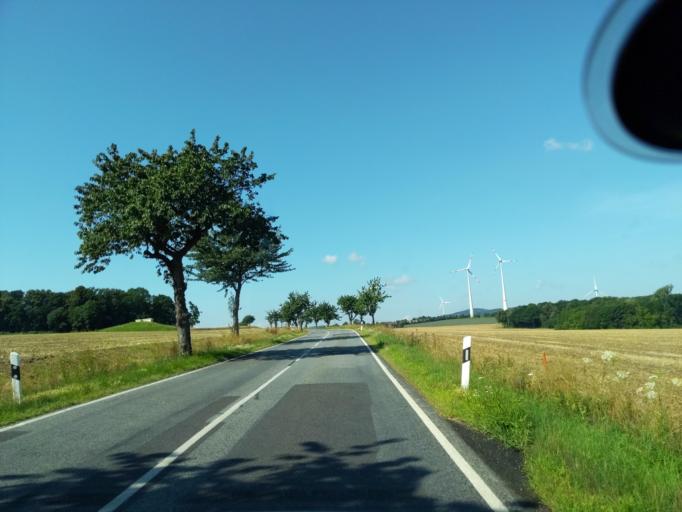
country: DE
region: Saxony
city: Lobau
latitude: 51.1290
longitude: 14.6720
